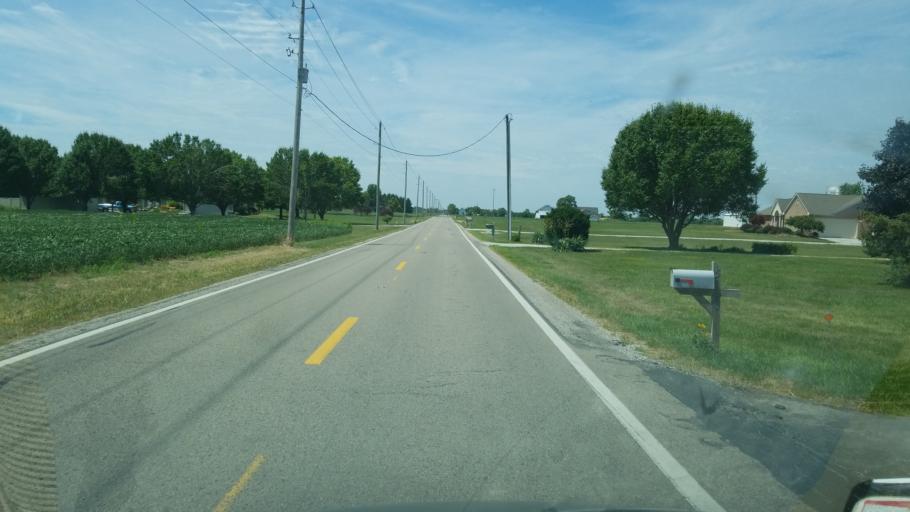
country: US
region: Ohio
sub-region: Franklin County
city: Grove City
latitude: 39.8602
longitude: -83.1311
